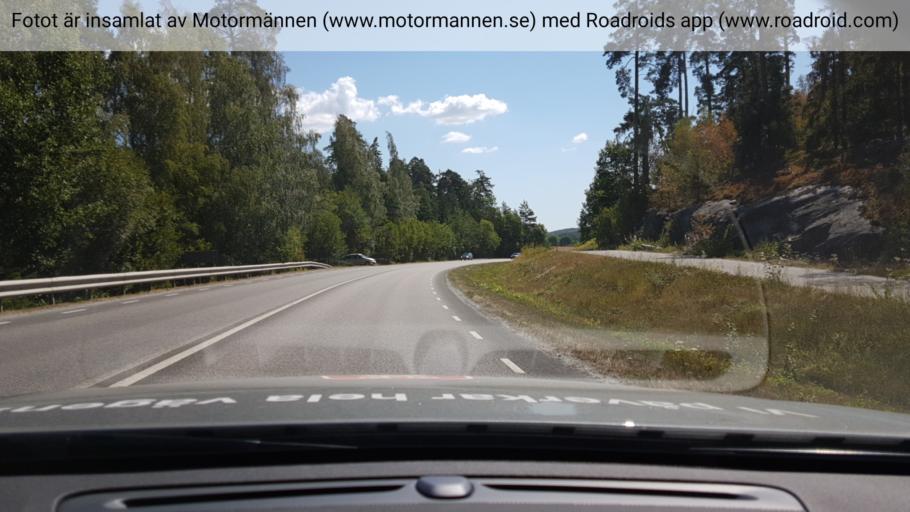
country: SE
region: Stockholm
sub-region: Ekero Kommun
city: Ekeroe
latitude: 59.3018
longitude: 17.8074
